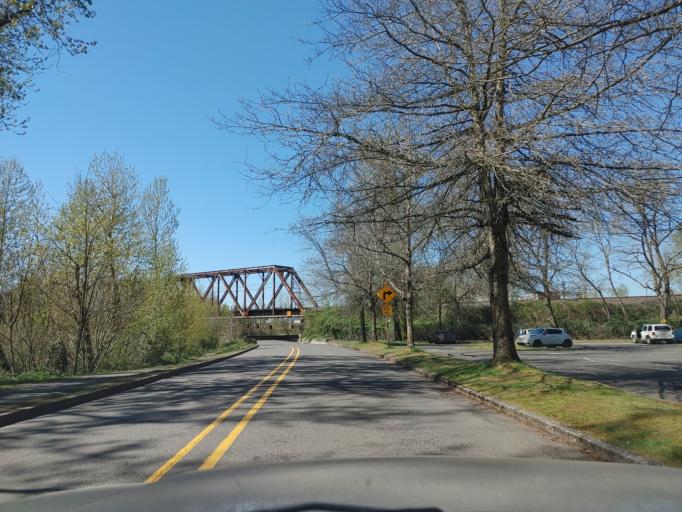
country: US
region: Oregon
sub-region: Multnomah County
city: Troutdale
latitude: 45.5414
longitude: -122.3804
